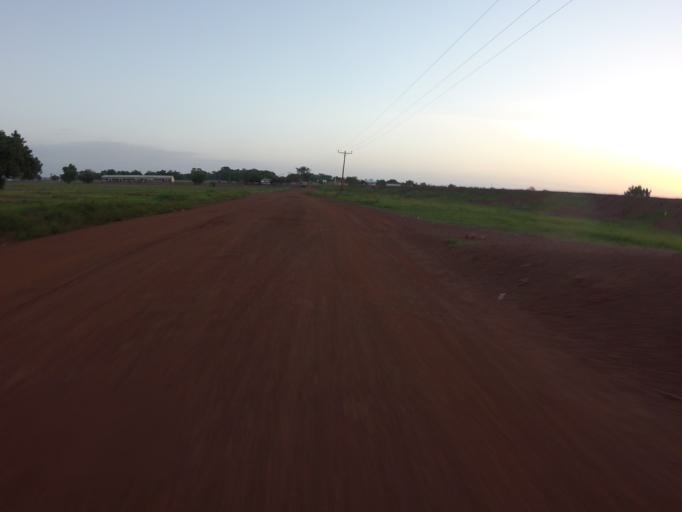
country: GH
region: Northern
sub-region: Yendi
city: Yendi
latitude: 9.9286
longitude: -0.2085
